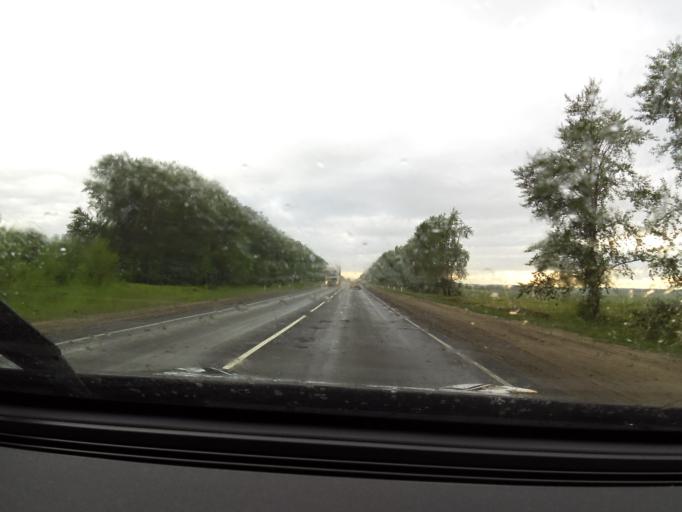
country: RU
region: Chuvashia
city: Yantikovo
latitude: 55.7890
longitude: 47.7252
